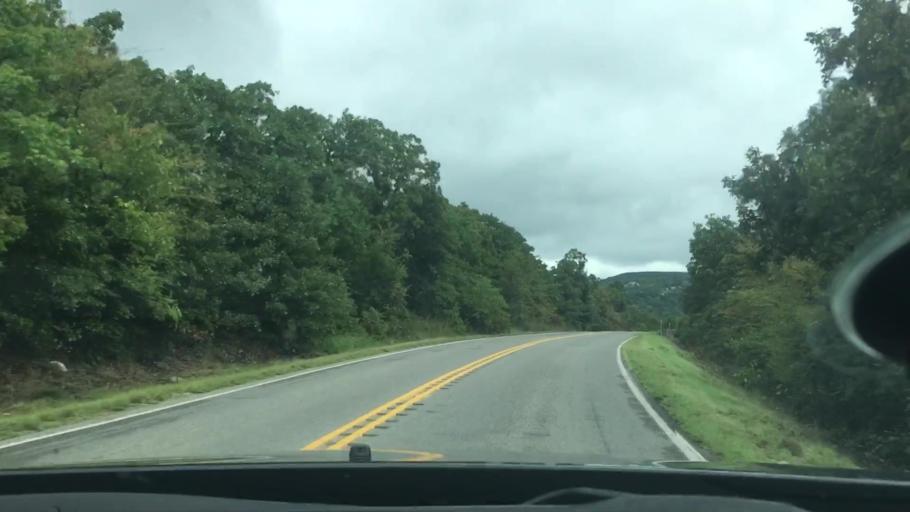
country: US
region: Oklahoma
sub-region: Sequoyah County
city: Vian
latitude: 35.6286
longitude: -94.9650
